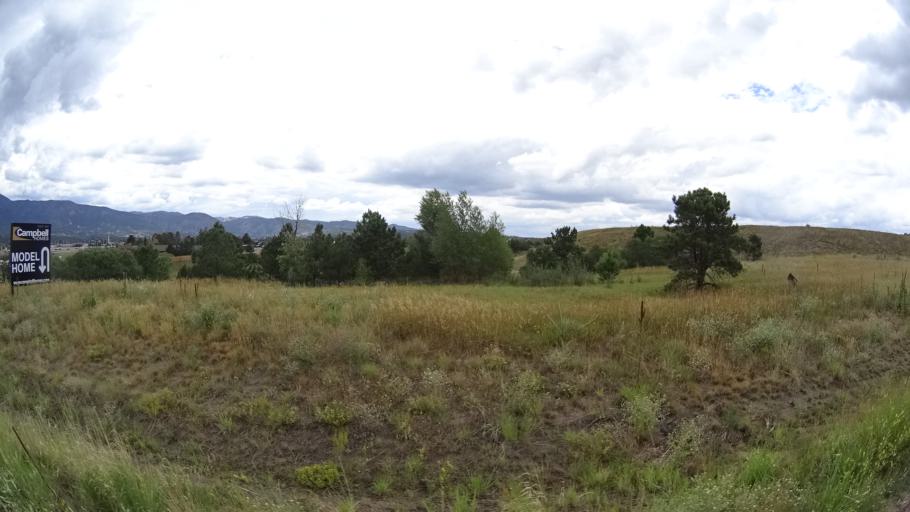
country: US
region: Colorado
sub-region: El Paso County
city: Woodmoor
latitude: 39.0962
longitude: -104.8578
